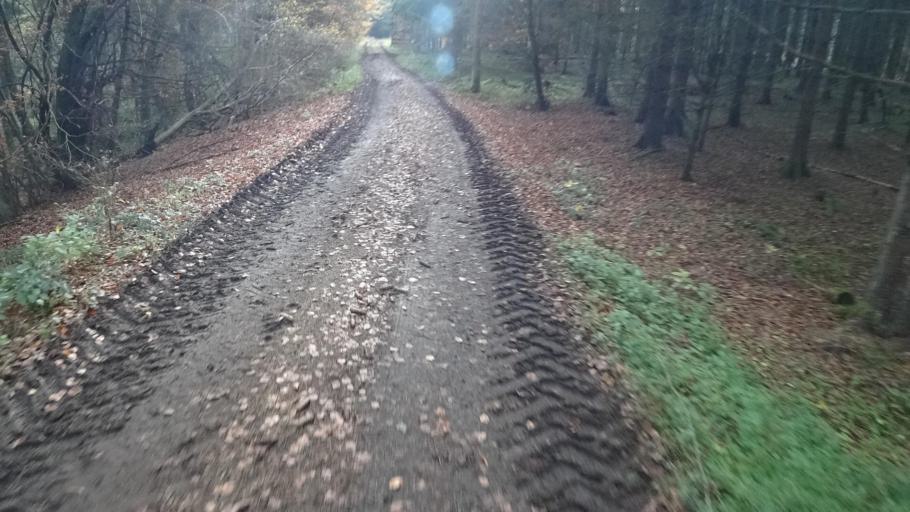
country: DE
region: Rheinland-Pfalz
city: Hausbay
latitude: 50.1024
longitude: 7.5369
